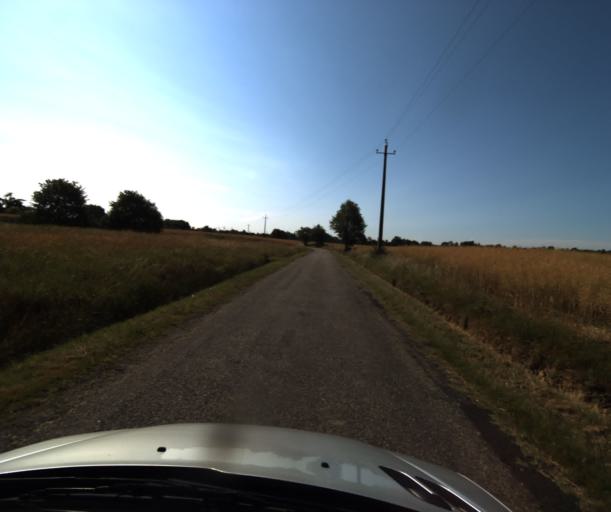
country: FR
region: Midi-Pyrenees
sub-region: Departement du Tarn-et-Garonne
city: Bressols
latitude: 43.9438
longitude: 1.2967
